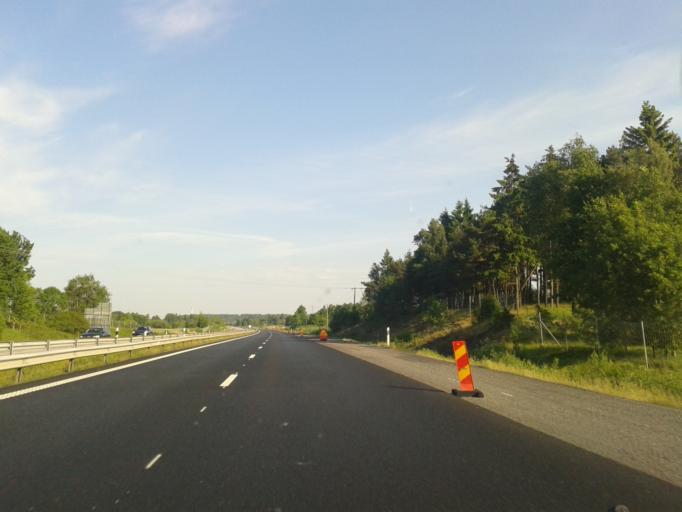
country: SE
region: Vaestra Goetaland
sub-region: Kungalvs Kommun
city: Kungalv
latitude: 57.8908
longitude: 11.9372
